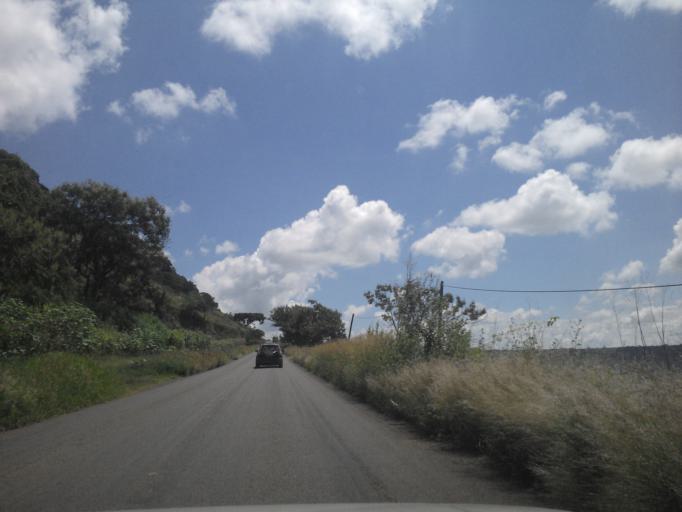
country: MX
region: Jalisco
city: Atotonilco el Alto
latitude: 20.5647
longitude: -102.5055
